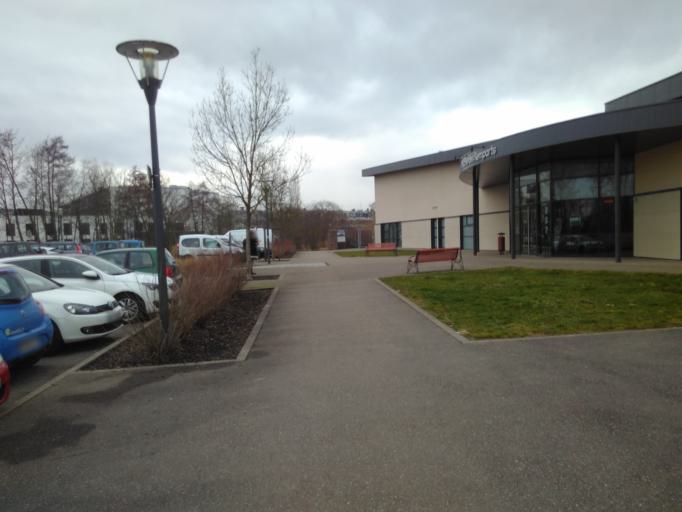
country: FR
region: Alsace
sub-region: Departement du Bas-Rhin
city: Selestat
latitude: 48.2536
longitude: 7.4530
